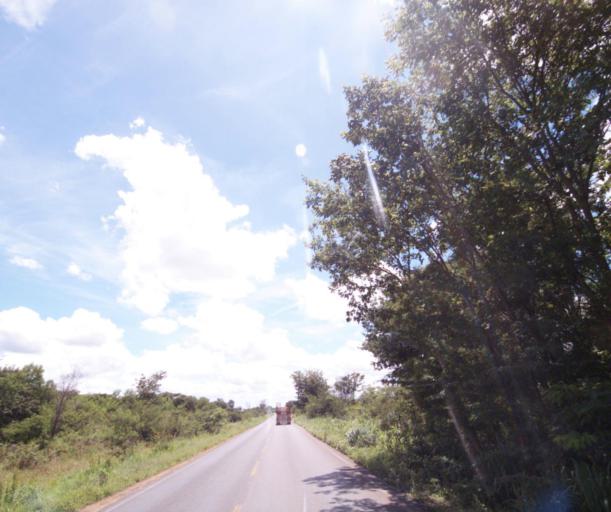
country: BR
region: Bahia
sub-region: Bom Jesus Da Lapa
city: Bom Jesus da Lapa
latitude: -13.2633
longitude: -43.5511
